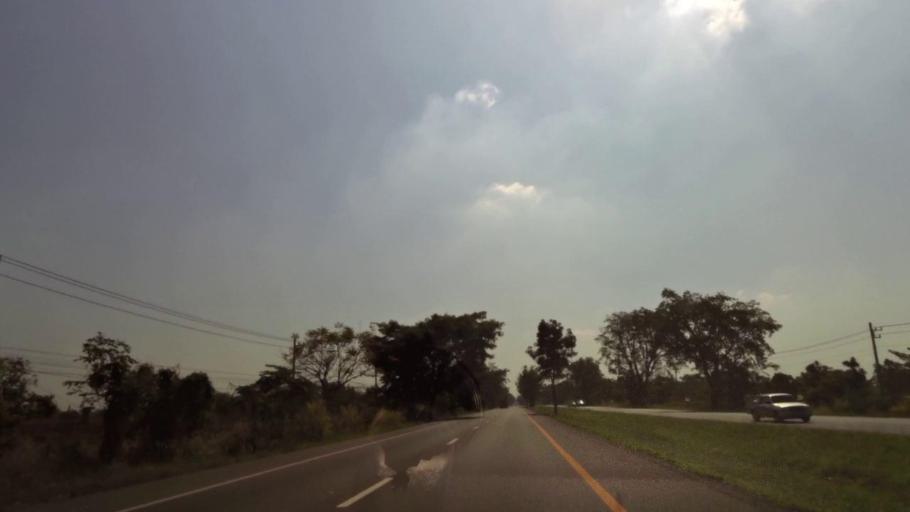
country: TH
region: Phichit
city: Bueng Na Rang
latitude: 16.2236
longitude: 100.1263
